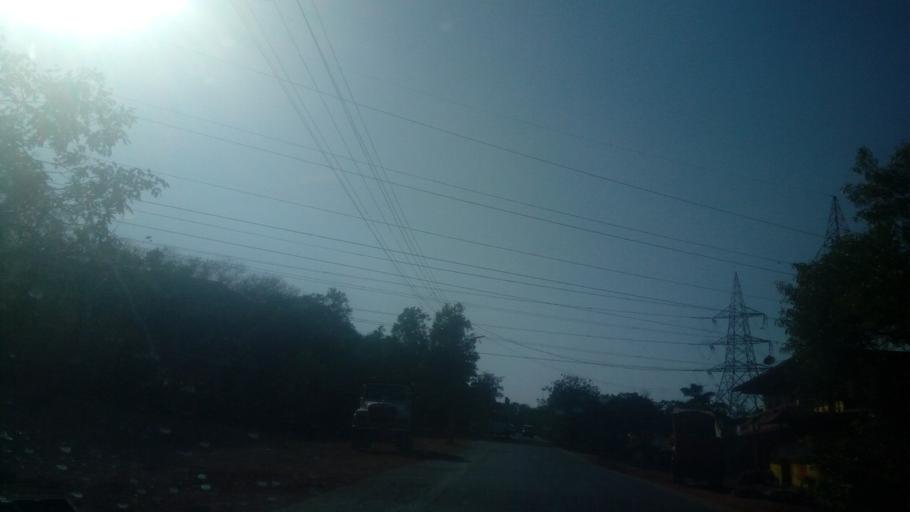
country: IN
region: Goa
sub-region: North Goa
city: Navelim
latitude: 15.5272
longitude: 73.9984
